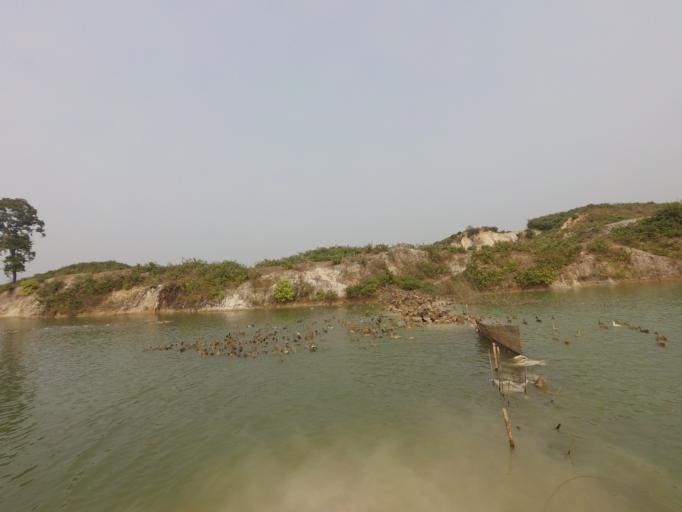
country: BD
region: Dhaka
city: Netrakona
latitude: 25.1576
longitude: 90.6420
